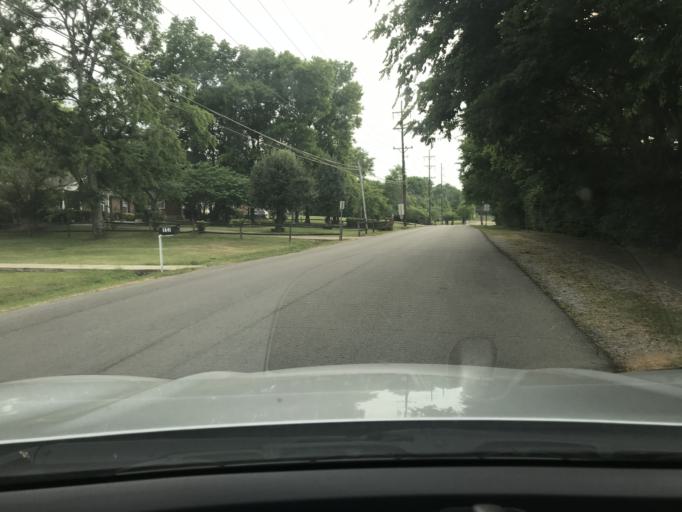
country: US
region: Tennessee
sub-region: Davidson County
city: Goodlettsville
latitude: 36.3129
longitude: -86.7113
